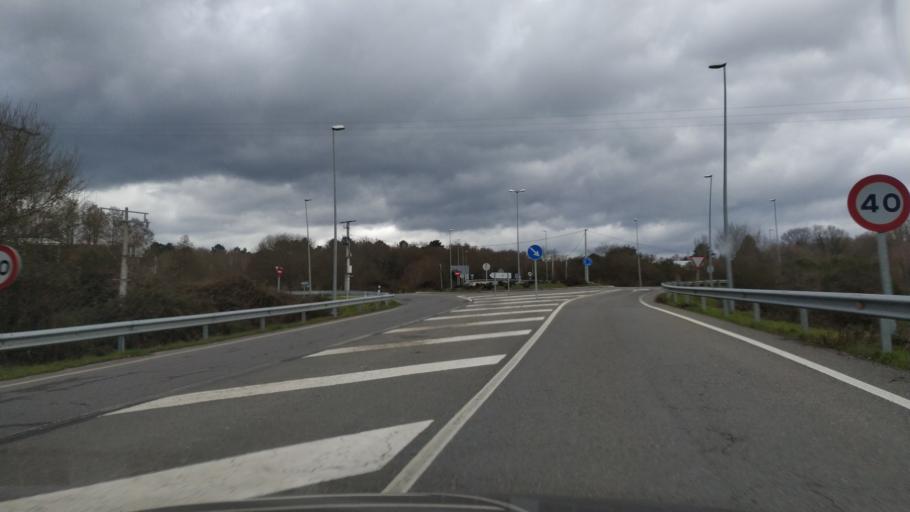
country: ES
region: Galicia
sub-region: Provincia de Ourense
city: Allariz
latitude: 42.2019
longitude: -7.8080
